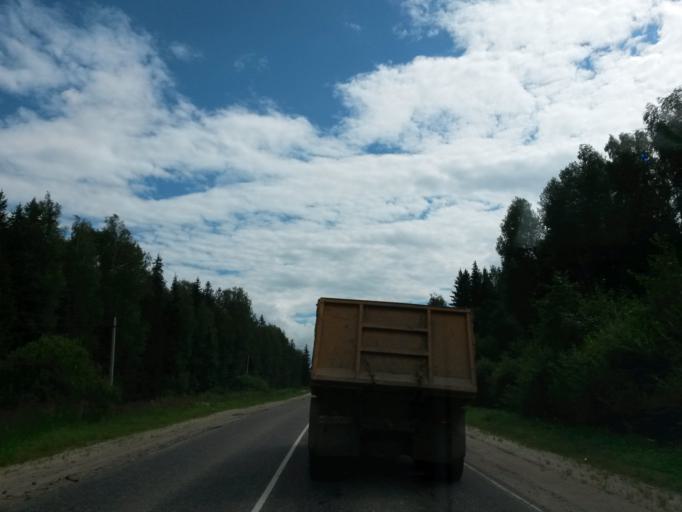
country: RU
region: Ivanovo
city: Novo-Talitsy
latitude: 57.0550
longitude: 40.7307
